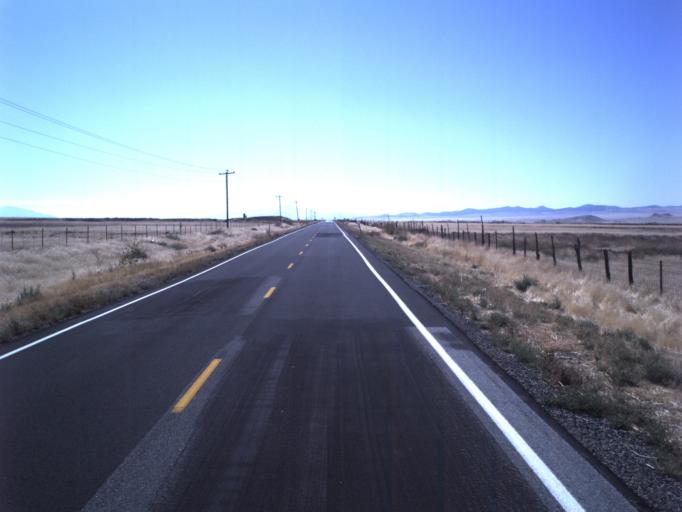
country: US
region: Utah
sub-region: Tooele County
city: Grantsville
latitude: 40.4280
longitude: -112.7488
